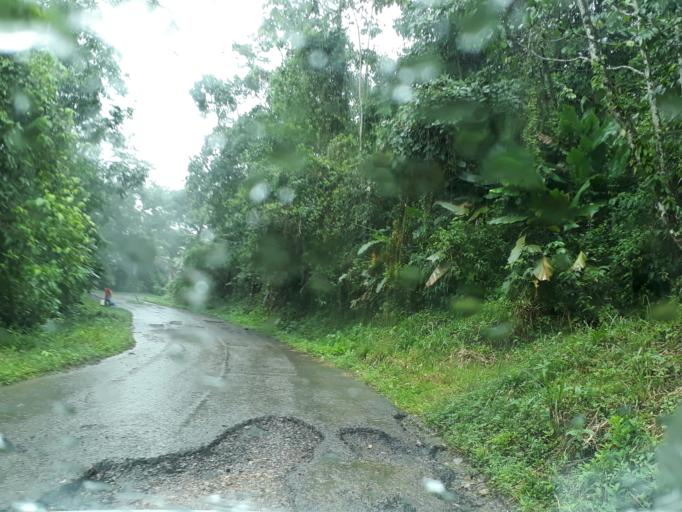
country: CO
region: Boyaca
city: Santa Maria
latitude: 4.7115
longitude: -73.2991
